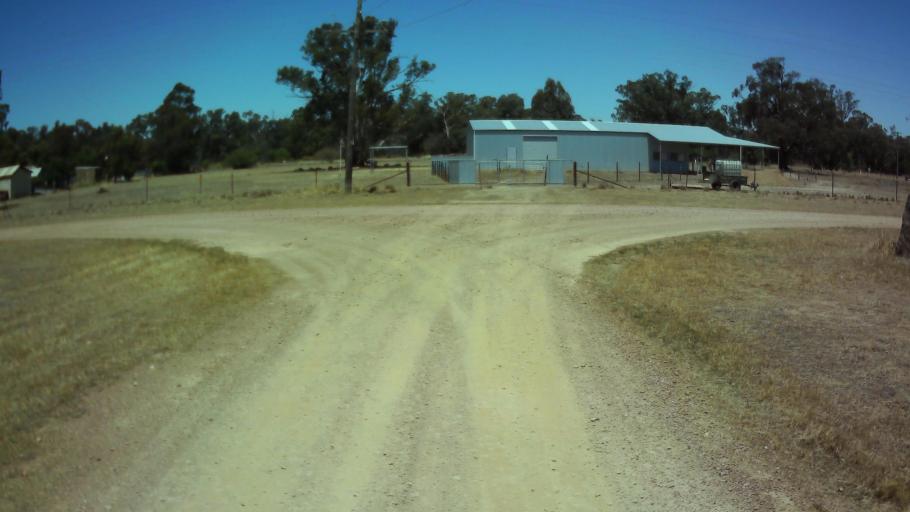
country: AU
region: New South Wales
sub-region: Weddin
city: Grenfell
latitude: -34.0373
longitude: 147.9285
